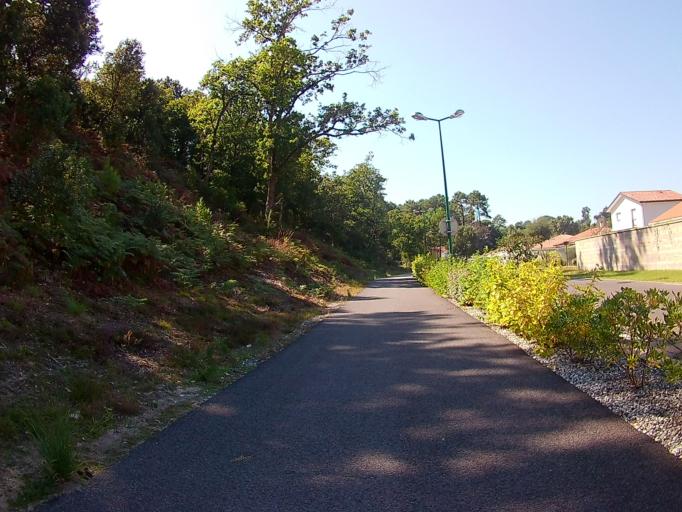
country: FR
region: Aquitaine
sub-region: Departement des Landes
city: Labenne
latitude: 43.5915
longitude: -1.4351
